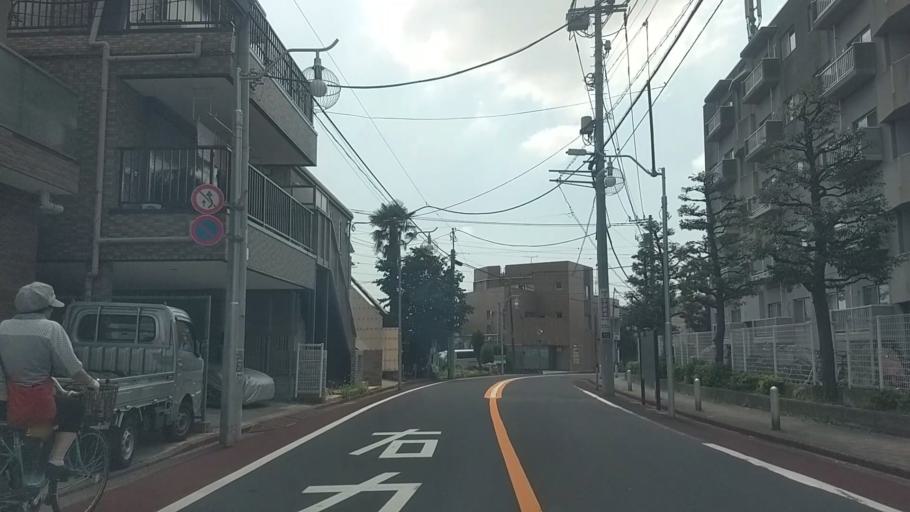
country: JP
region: Kanagawa
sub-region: Kawasaki-shi
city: Kawasaki
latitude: 35.5873
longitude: 139.7141
